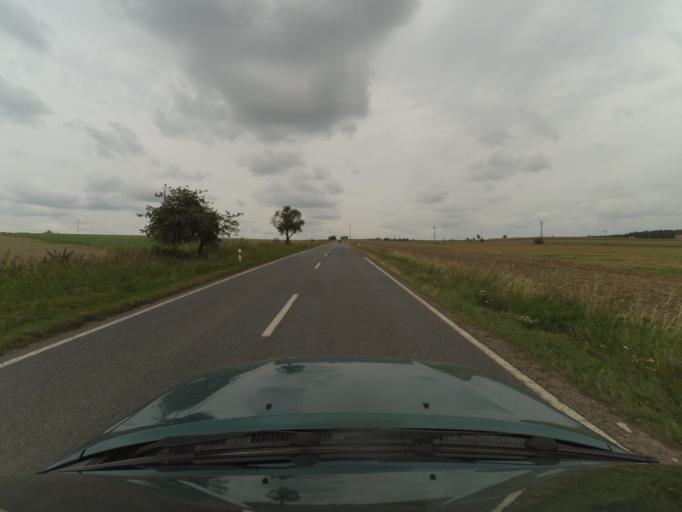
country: CZ
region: Plzensky
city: Kozlany
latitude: 50.0334
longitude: 13.5956
